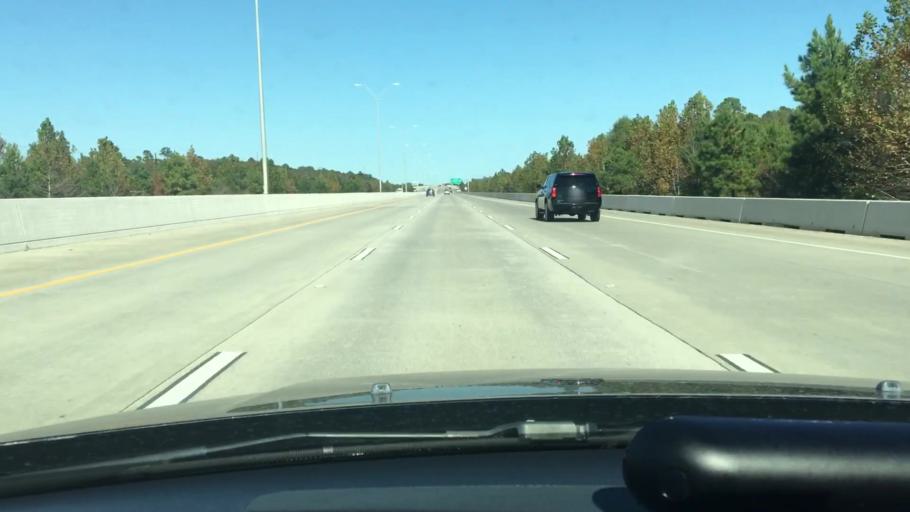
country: US
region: Texas
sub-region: Harris County
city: Sheldon
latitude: 29.8603
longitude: -95.1870
